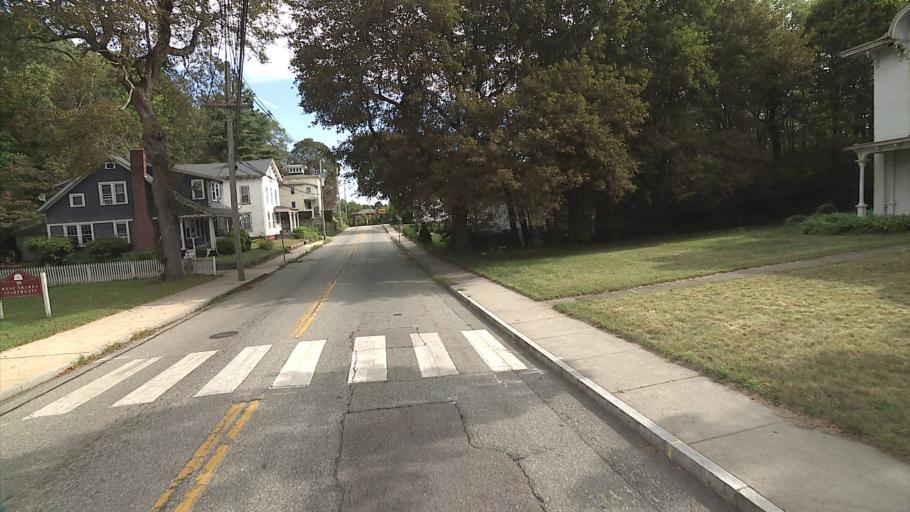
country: US
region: Connecticut
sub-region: New London County
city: Norwich
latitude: 41.5152
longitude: -72.0810
